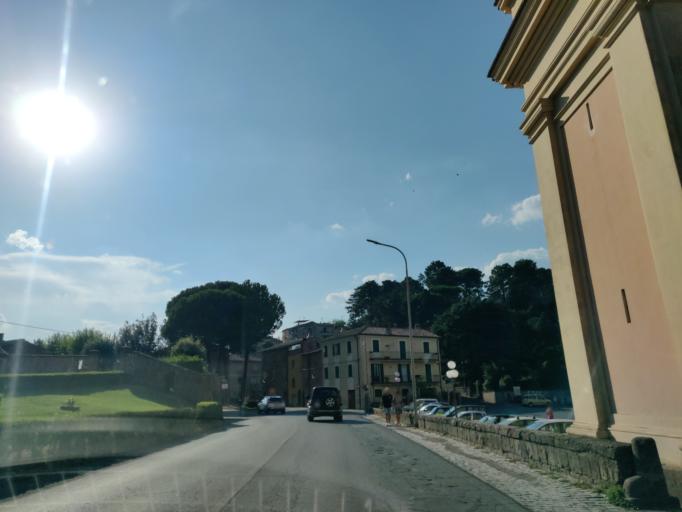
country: IT
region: Latium
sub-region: Provincia di Viterbo
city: Acquapendente
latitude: 42.7425
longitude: 11.8710
